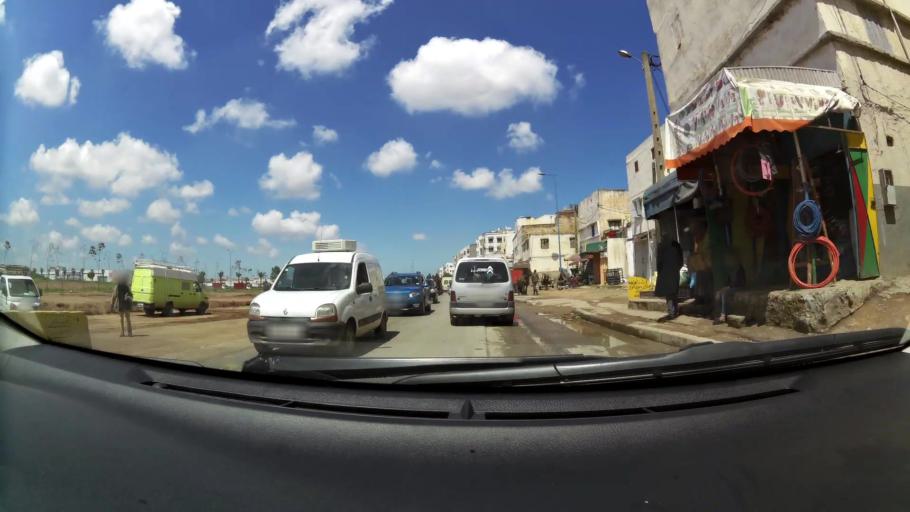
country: MA
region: Grand Casablanca
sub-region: Mediouna
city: Tit Mellil
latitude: 33.5460
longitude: -7.5453
